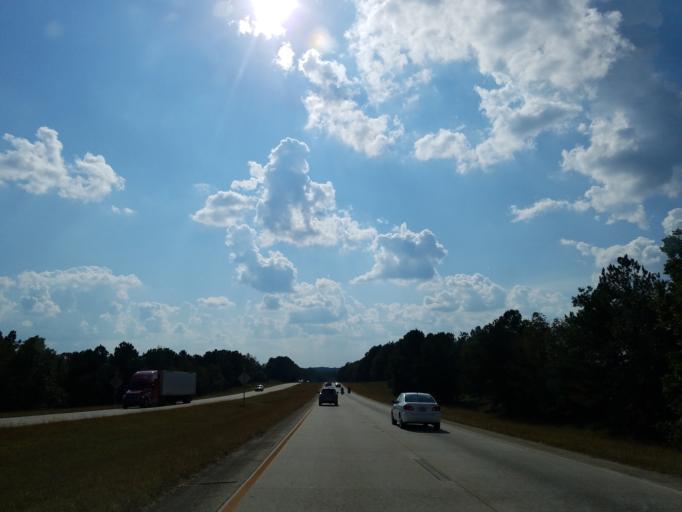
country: US
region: Georgia
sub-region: Barrow County
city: Russell
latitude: 33.9551
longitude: -83.6588
